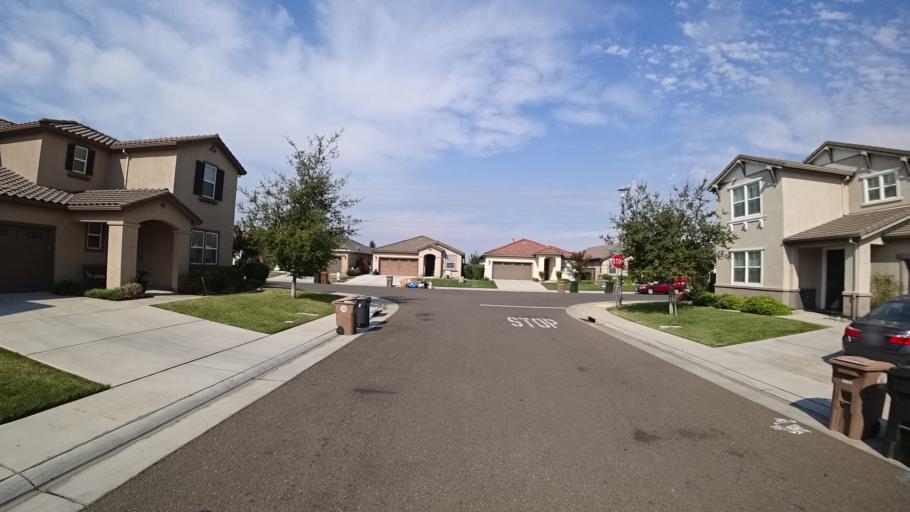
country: US
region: California
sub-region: Sacramento County
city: Laguna
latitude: 38.3780
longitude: -121.4494
